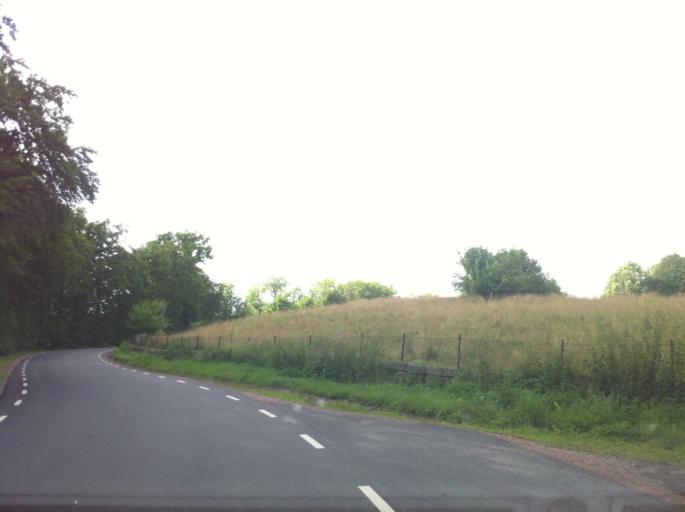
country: SE
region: Skane
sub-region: Trelleborgs Kommun
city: Anderslov
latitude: 55.4762
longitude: 13.3647
